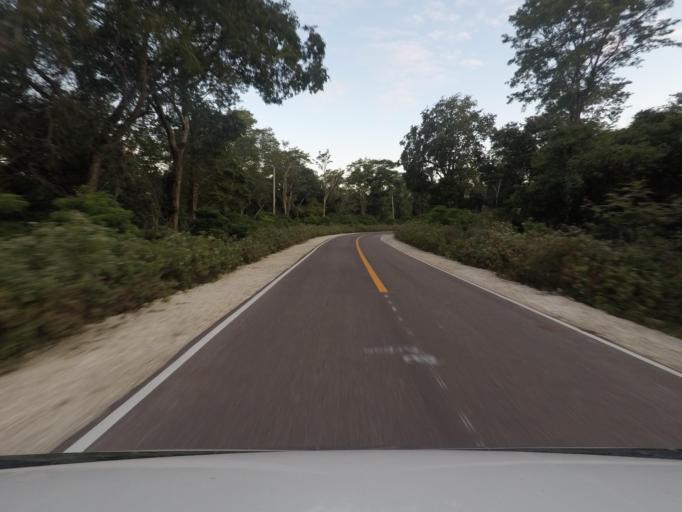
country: TL
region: Lautem
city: Lospalos
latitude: -8.4054
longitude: 127.2890
